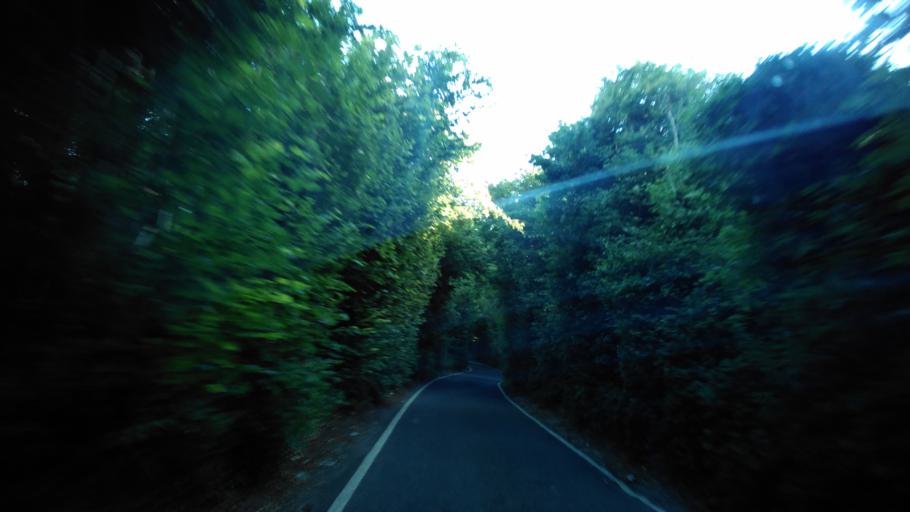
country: GB
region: England
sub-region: Kent
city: Chartham
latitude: 51.2625
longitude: 1.0153
